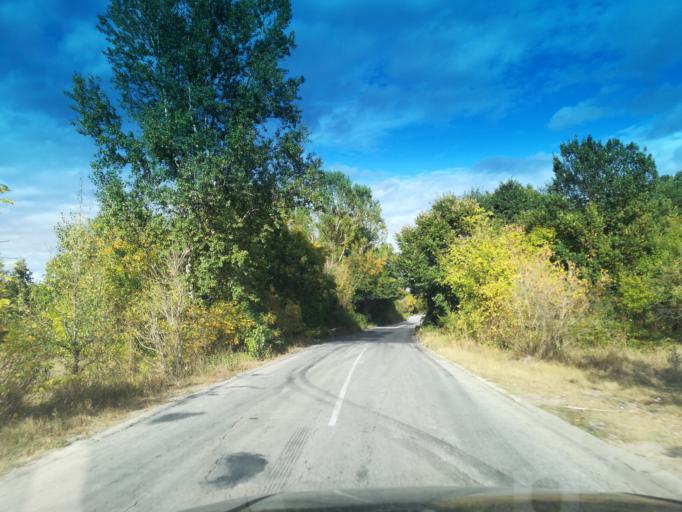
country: BG
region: Pazardzhik
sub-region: Obshtina Bratsigovo
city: Bratsigovo
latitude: 42.0581
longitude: 24.3470
